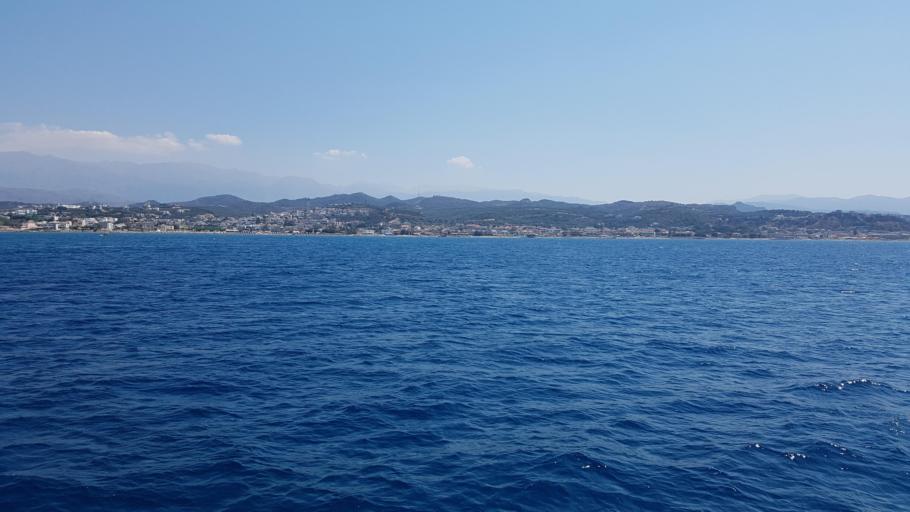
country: GR
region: Crete
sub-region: Nomos Chanias
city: Agia Marina
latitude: 35.5308
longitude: 23.9246
